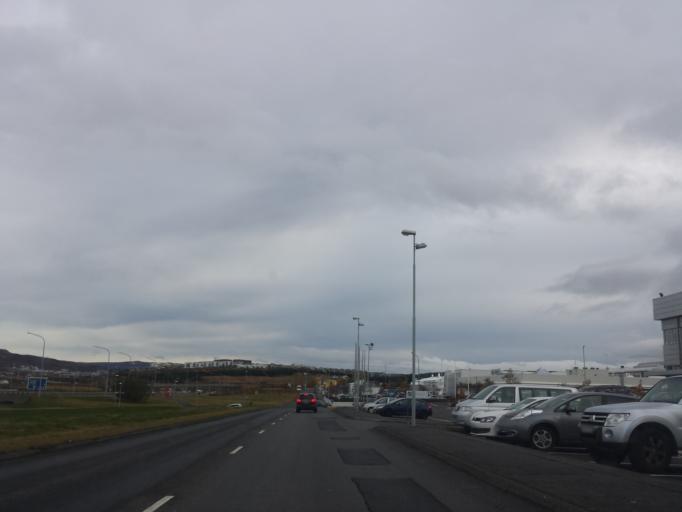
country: IS
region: Capital Region
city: Reykjavik
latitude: 64.1237
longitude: -21.7990
